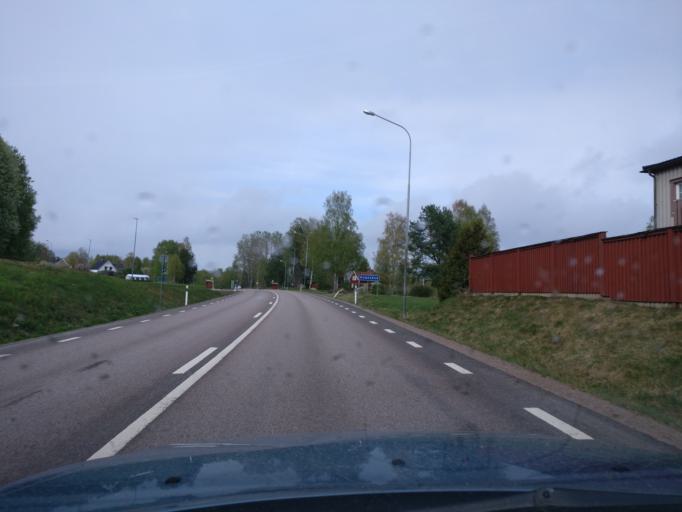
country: SE
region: Vaermland
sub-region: Munkfors Kommun
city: Munkfors
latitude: 59.8204
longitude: 13.5180
